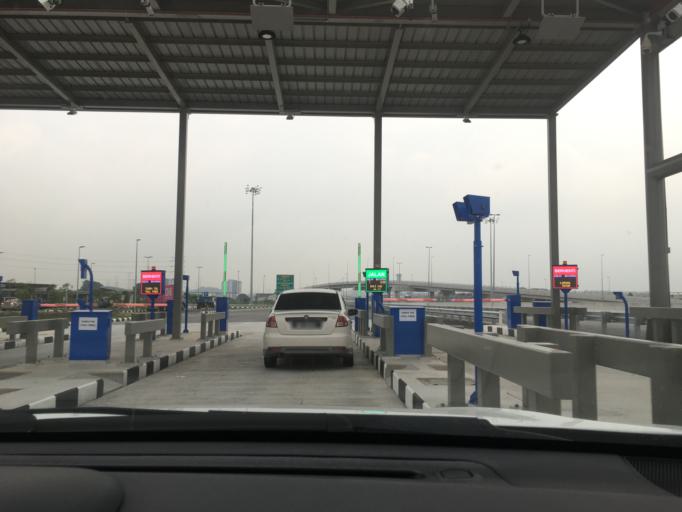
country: MY
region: Selangor
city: Klang
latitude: 3.0943
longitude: 101.4375
